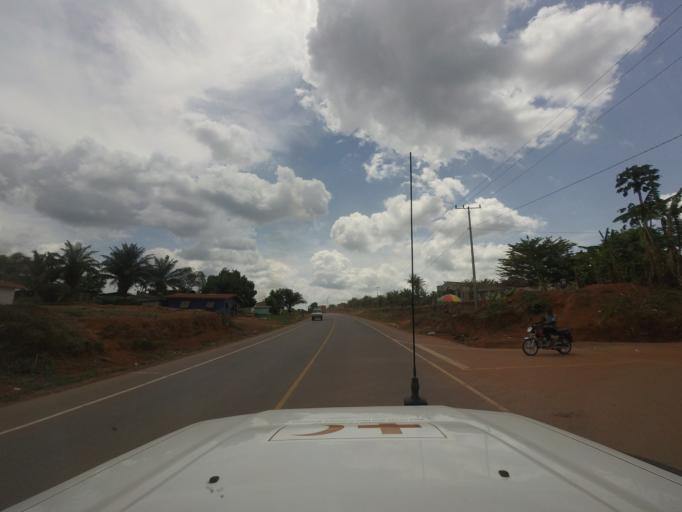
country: LR
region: Nimba
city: Sanniquellie
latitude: 7.2306
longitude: -8.9994
